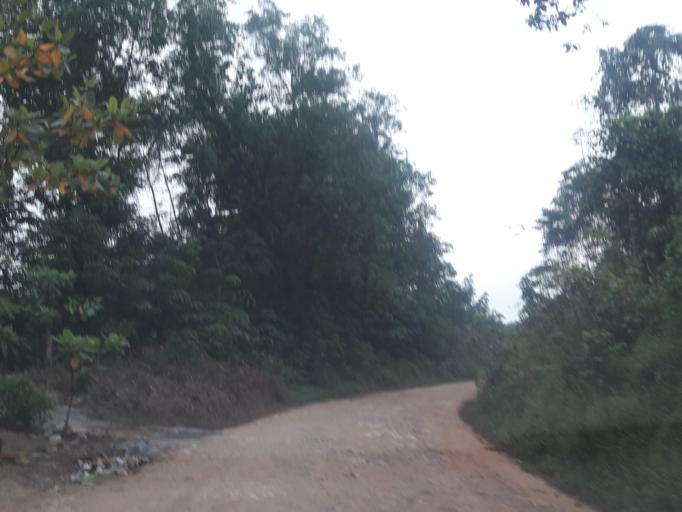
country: ID
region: South Kalimantan
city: Tanjung
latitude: -2.1346
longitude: 115.4525
